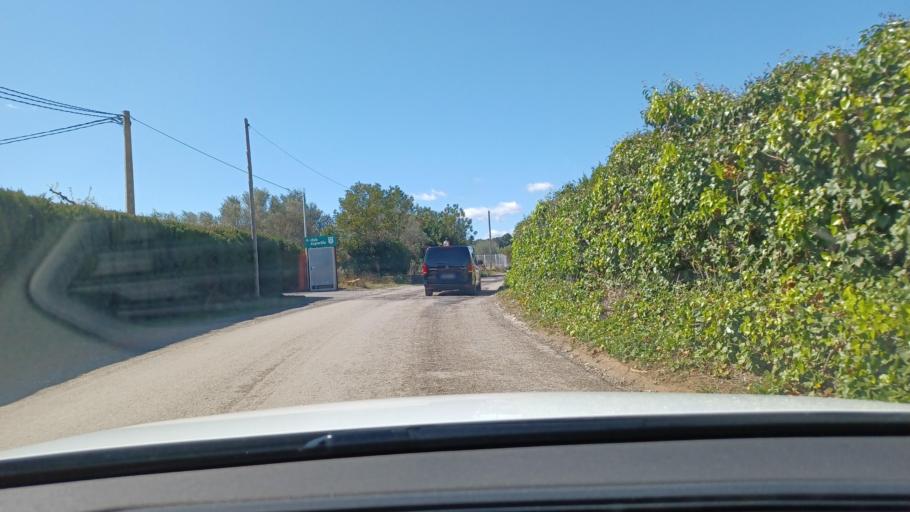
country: ES
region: Catalonia
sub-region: Provincia de Tarragona
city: Masdenverge
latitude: 40.6962
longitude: 0.5497
